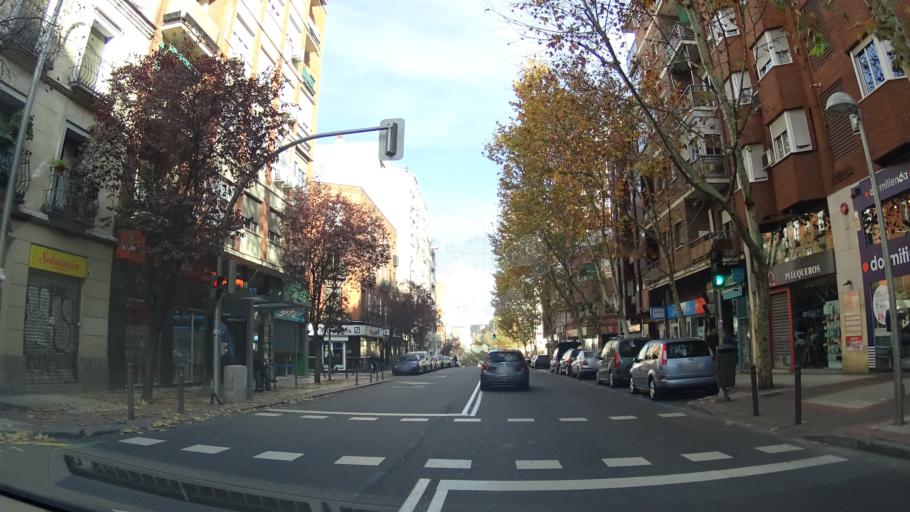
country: ES
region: Madrid
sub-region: Provincia de Madrid
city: Chamartin
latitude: 40.4456
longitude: -3.6718
